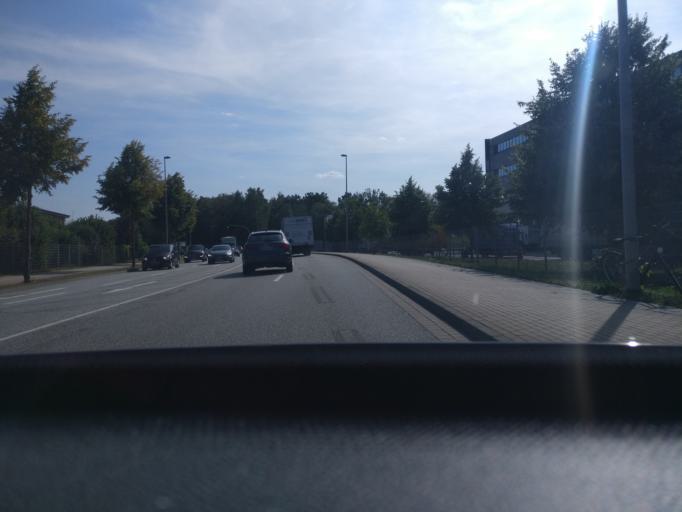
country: DE
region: Hamburg
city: Langenhorn
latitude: 53.6587
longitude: 9.9804
